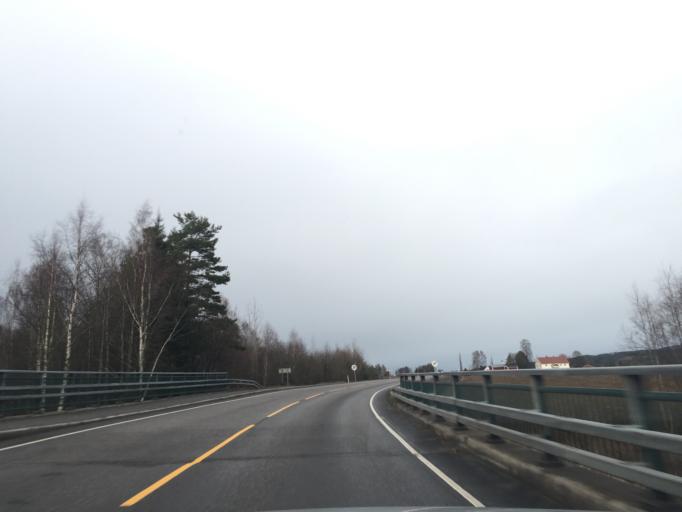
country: NO
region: Hedmark
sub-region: Asnes
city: Flisa
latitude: 60.5834
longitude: 12.0489
